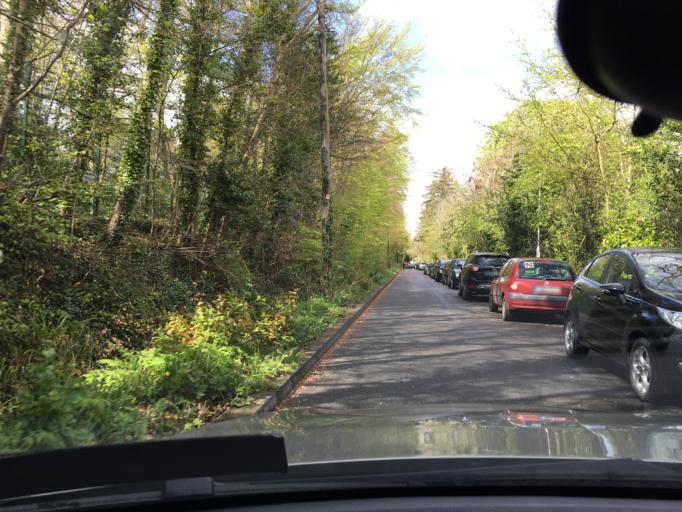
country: IE
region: Leinster
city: Castleknock
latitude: 53.3664
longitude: -6.3534
